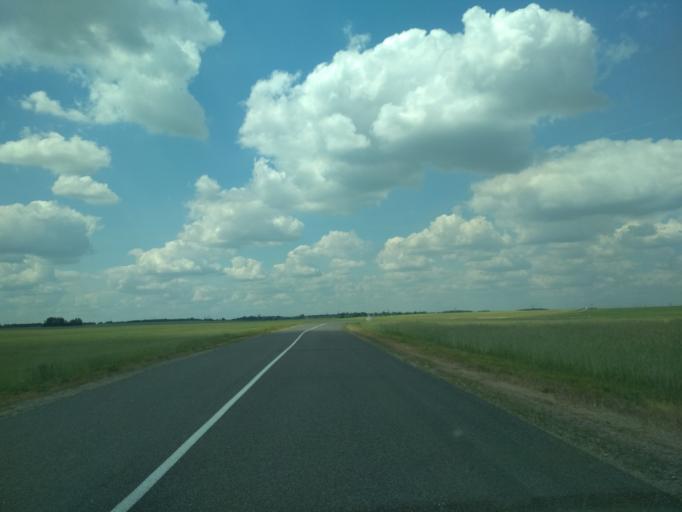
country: BY
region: Minsk
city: Mar''ina Horka
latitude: 53.5534
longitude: 28.1140
